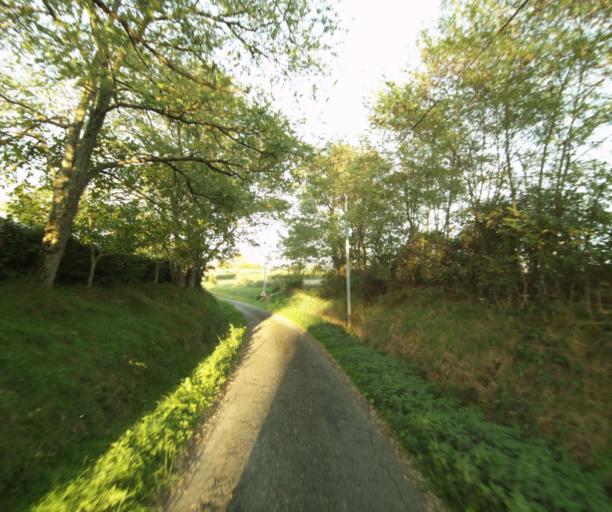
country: FR
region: Midi-Pyrenees
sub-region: Departement du Gers
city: Eauze
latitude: 43.8890
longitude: 0.0648
